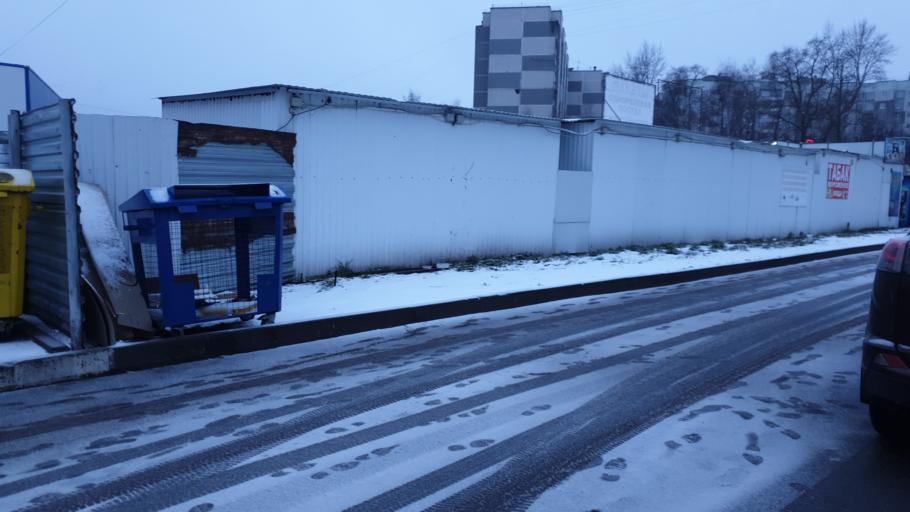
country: RU
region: Kursk
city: Kursk
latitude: 51.7305
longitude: 36.1437
